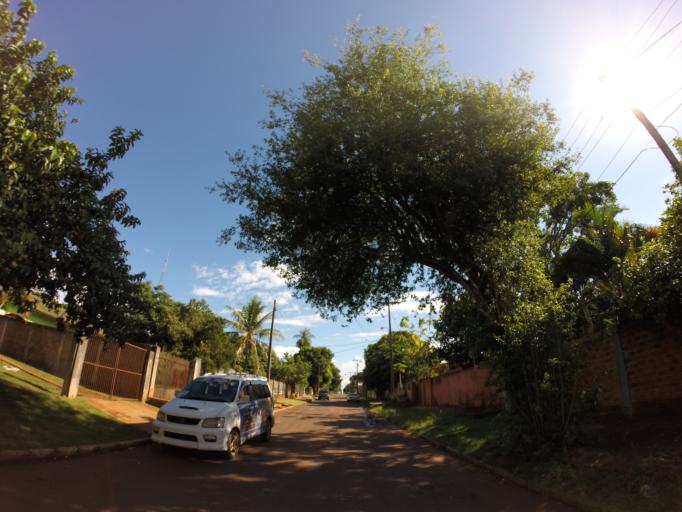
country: PY
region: Alto Parana
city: Ciudad del Este
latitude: -25.4010
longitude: -54.6243
